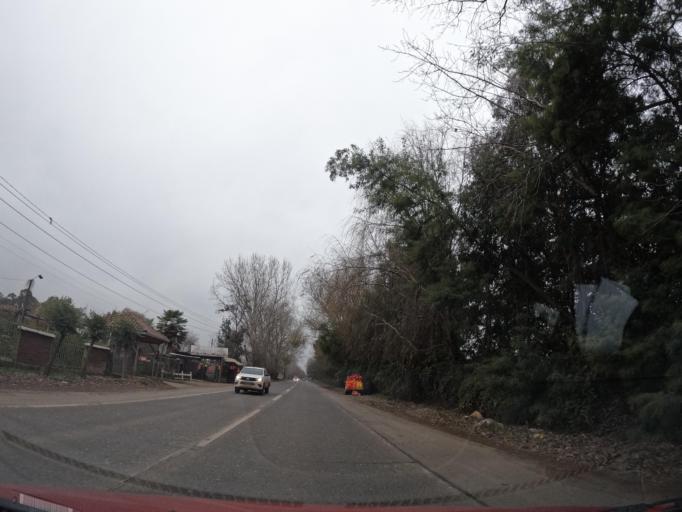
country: CL
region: Maule
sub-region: Provincia de Talca
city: San Clemente
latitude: -35.5552
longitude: -71.4673
